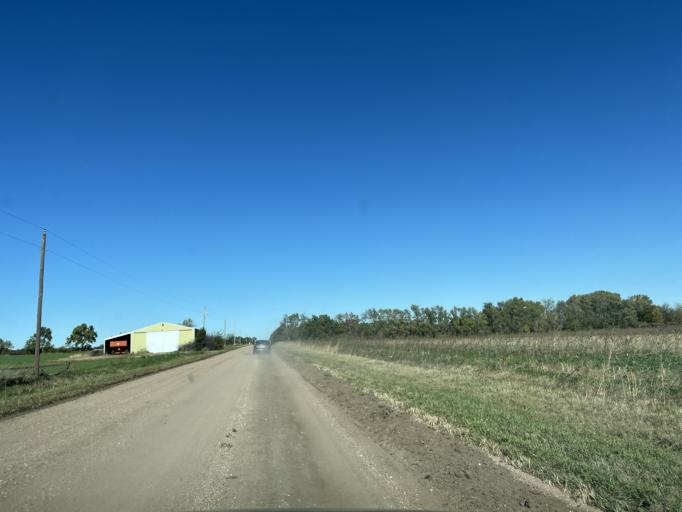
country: US
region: Kansas
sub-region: McPherson County
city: Moundridge
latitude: 38.2086
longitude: -97.6292
